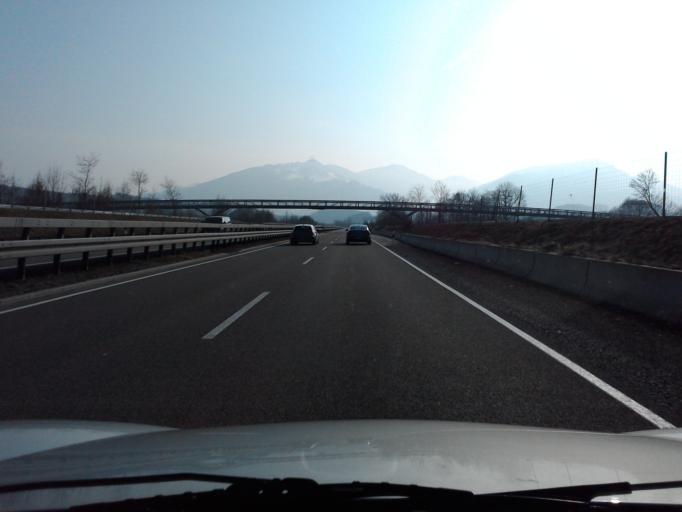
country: DE
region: Bavaria
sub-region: Swabia
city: Rettenberg
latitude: 47.5855
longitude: 10.2547
